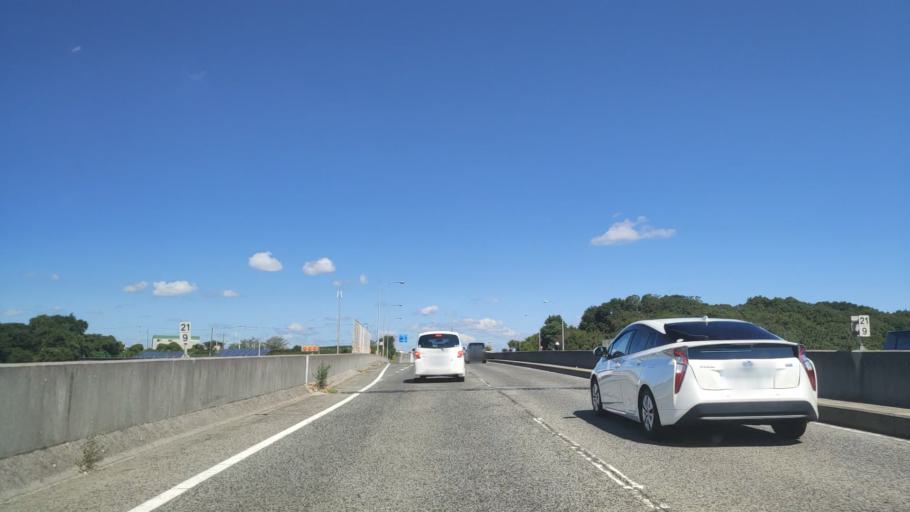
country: JP
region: Hyogo
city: Ono
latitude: 34.8346
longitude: 134.9482
